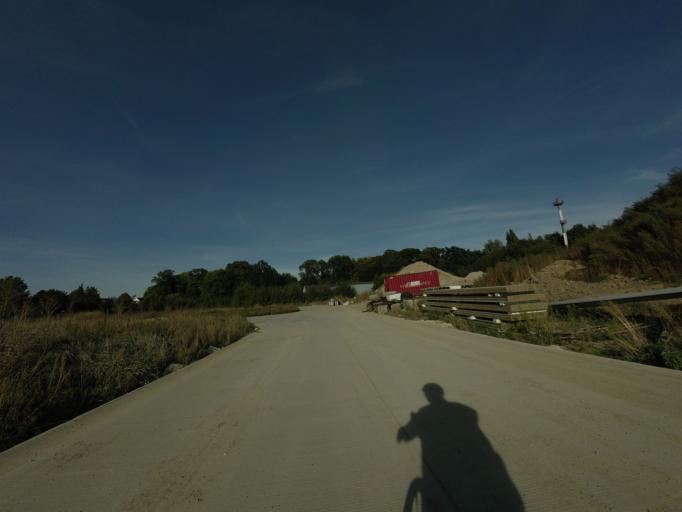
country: BE
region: Flanders
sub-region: Provincie Vlaams-Brabant
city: Steenokkerzeel
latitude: 50.9159
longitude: 4.4890
